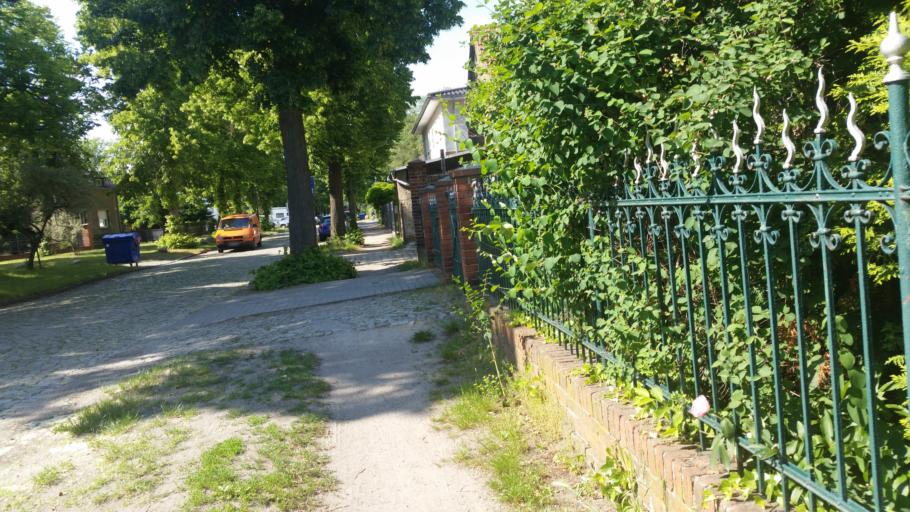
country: DE
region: Brandenburg
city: Zeuthen
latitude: 52.3503
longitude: 13.6331
